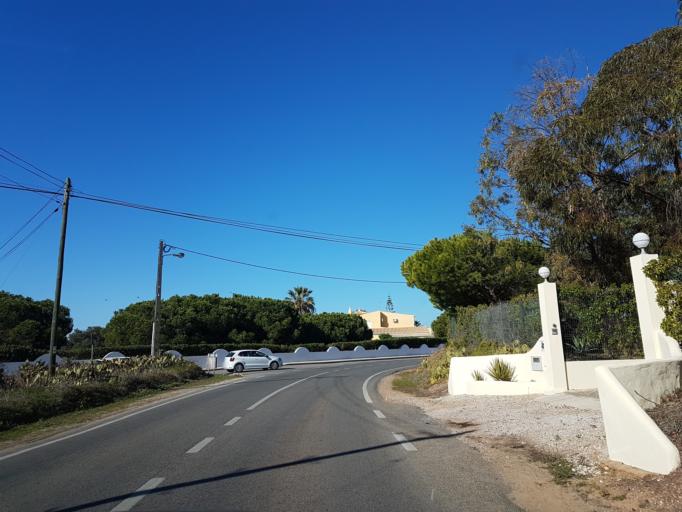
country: PT
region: Faro
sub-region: Lagoa
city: Carvoeiro
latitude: 37.0982
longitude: -8.4419
